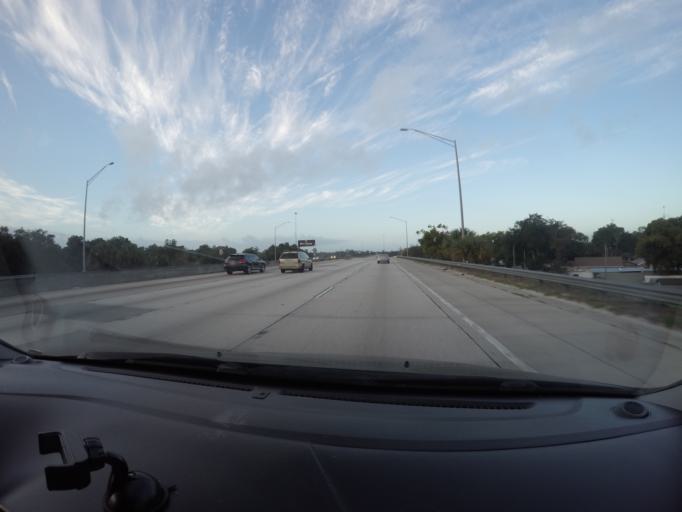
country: US
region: Florida
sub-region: Orange County
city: Holden Heights
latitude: 28.5139
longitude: -81.3915
